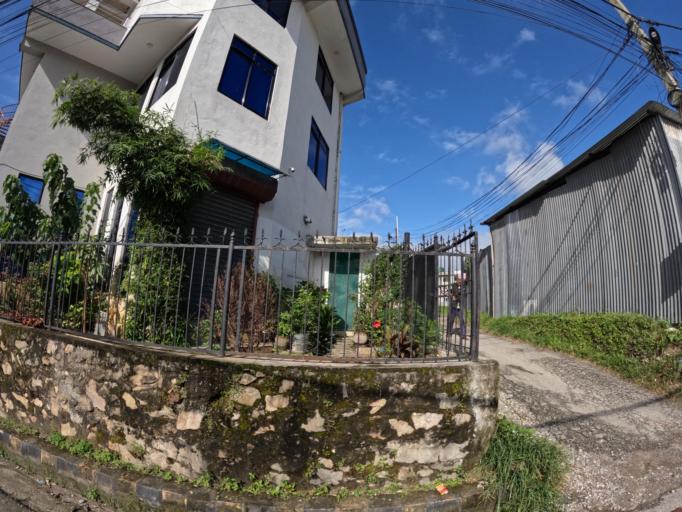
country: NP
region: Central Region
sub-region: Bagmati Zone
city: Kathmandu
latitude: 27.7606
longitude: 85.3332
